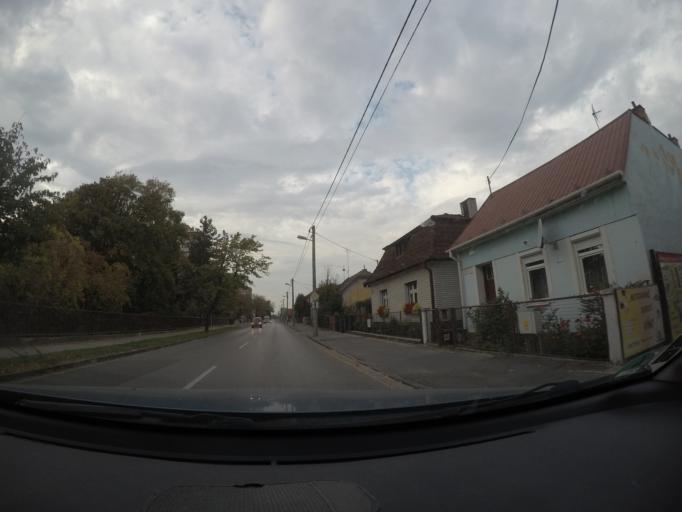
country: SK
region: Trenciansky
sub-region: Okres Trencin
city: Trencin
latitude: 48.8823
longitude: 18.0295
